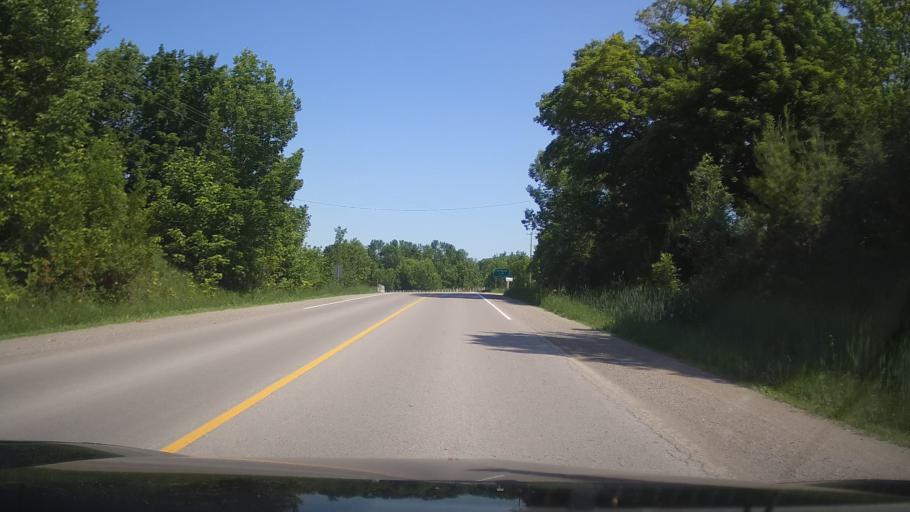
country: CA
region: Ontario
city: Orillia
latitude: 44.6369
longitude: -79.1022
